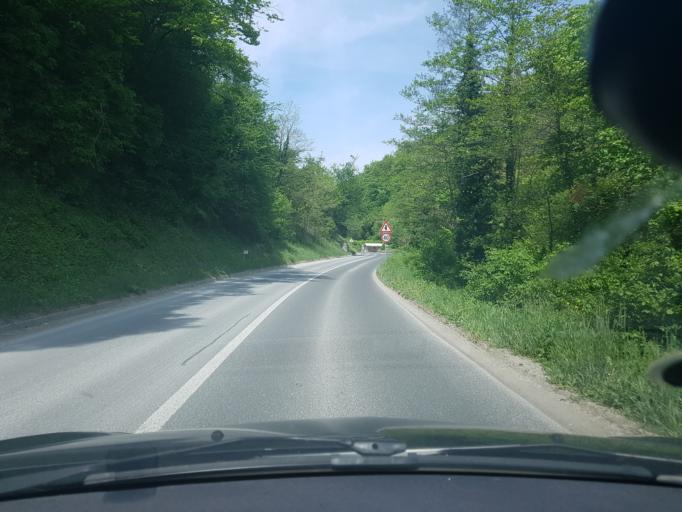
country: HR
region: Krapinsko-Zagorska
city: Pregrada
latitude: 46.1736
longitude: 15.7538
